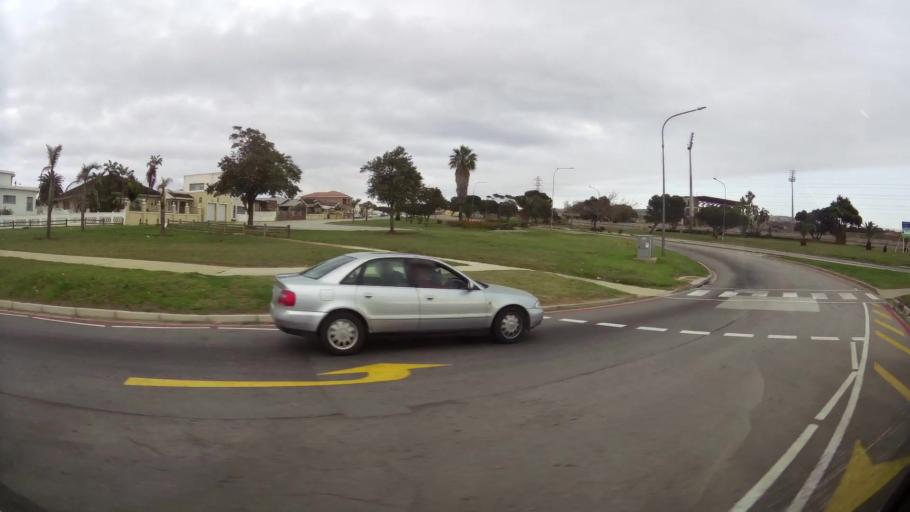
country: ZA
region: Eastern Cape
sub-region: Nelson Mandela Bay Metropolitan Municipality
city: Port Elizabeth
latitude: -33.9152
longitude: 25.5626
